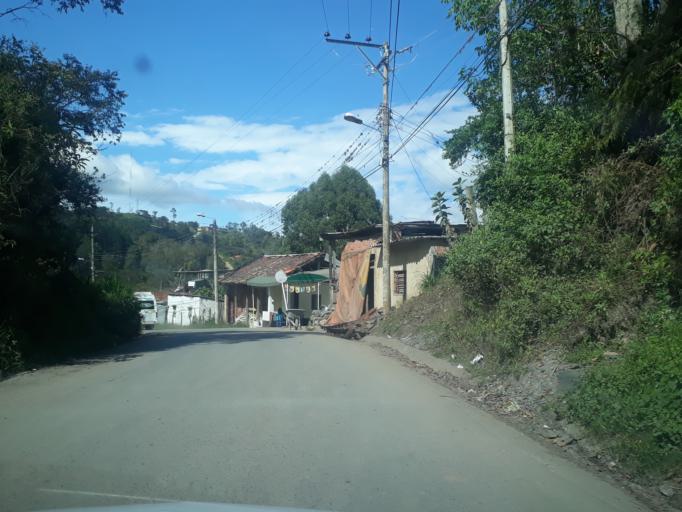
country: CO
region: Santander
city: Velez
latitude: 6.0199
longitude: -73.6694
